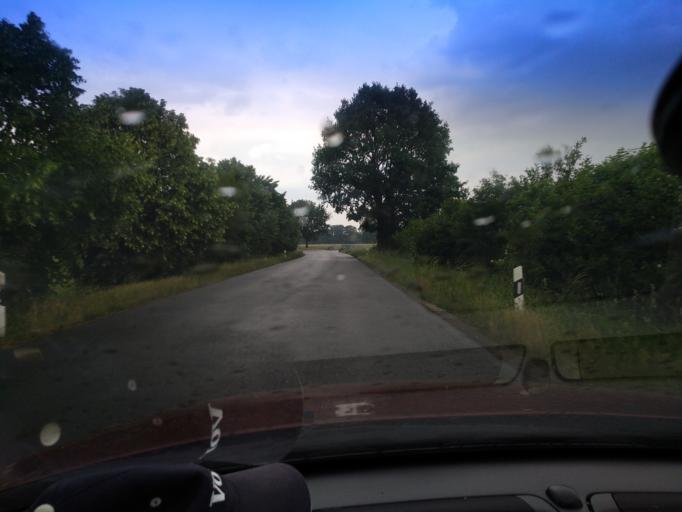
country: DE
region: Saxony
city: Klitten
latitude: 51.3542
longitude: 14.5856
